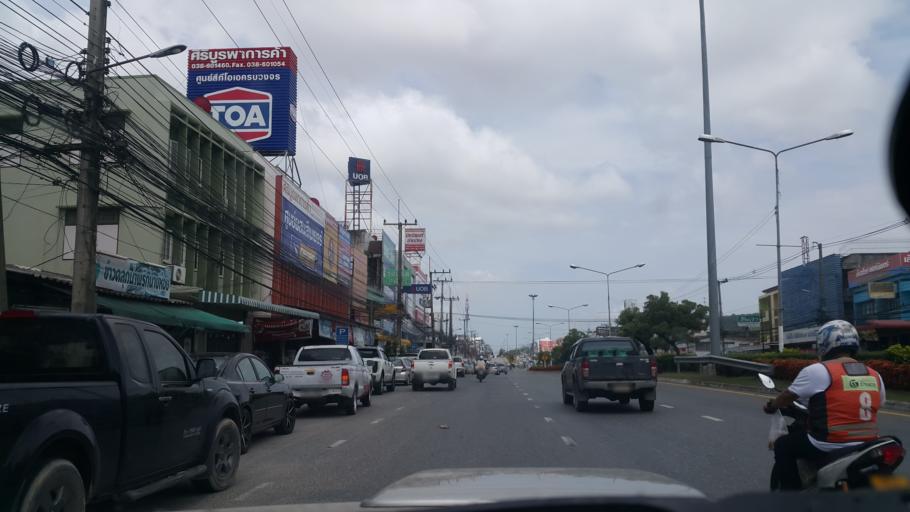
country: TH
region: Rayong
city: Ban Chang
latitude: 12.7237
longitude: 101.0532
